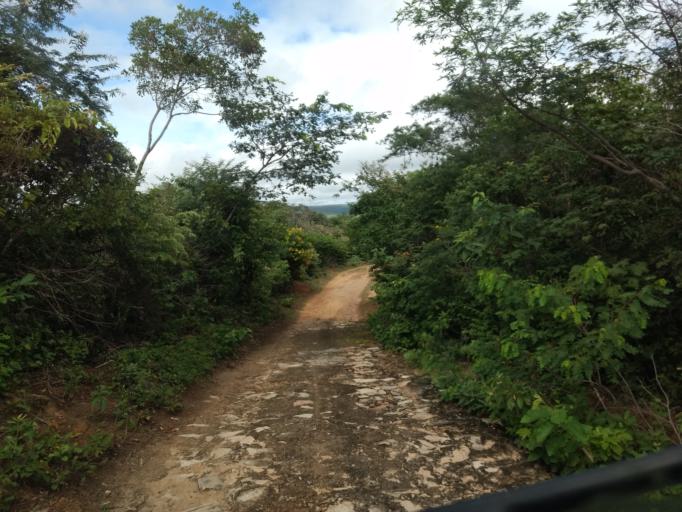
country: BR
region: Ceara
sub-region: Crateus
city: Crateus
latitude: -5.1927
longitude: -40.9495
